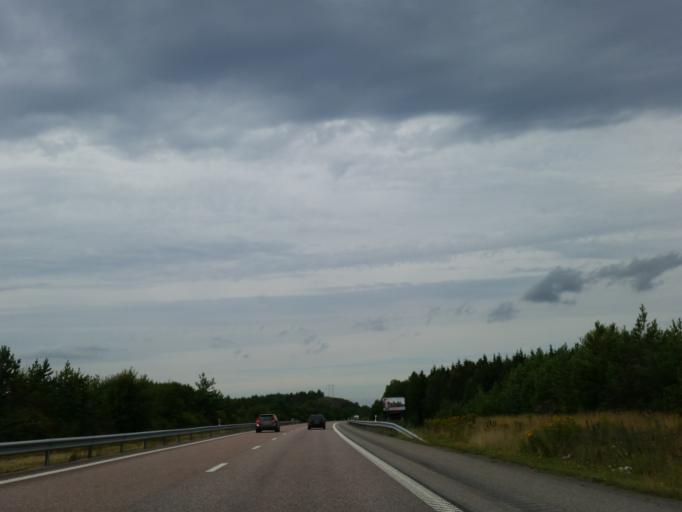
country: SE
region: Soedermanland
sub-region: Strangnas Kommun
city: Mariefred
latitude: 59.2312
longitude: 17.2007
